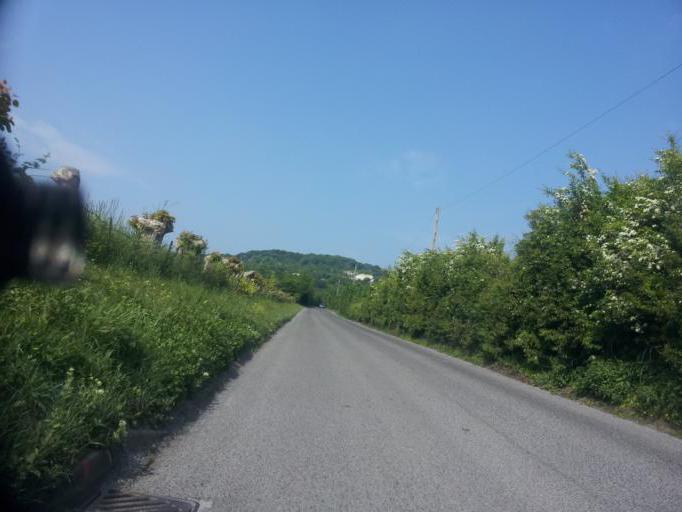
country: GB
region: England
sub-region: Kent
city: Aylesford
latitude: 51.3135
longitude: 0.4966
